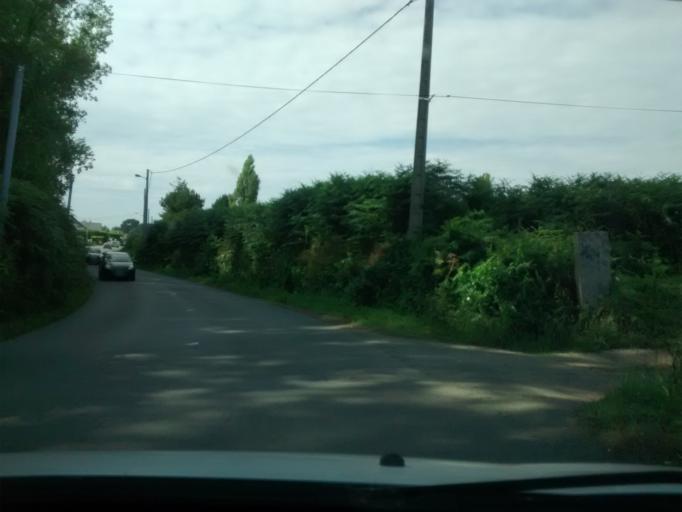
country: FR
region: Brittany
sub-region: Departement des Cotes-d'Armor
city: Penvenan
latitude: 48.8207
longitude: -3.2988
